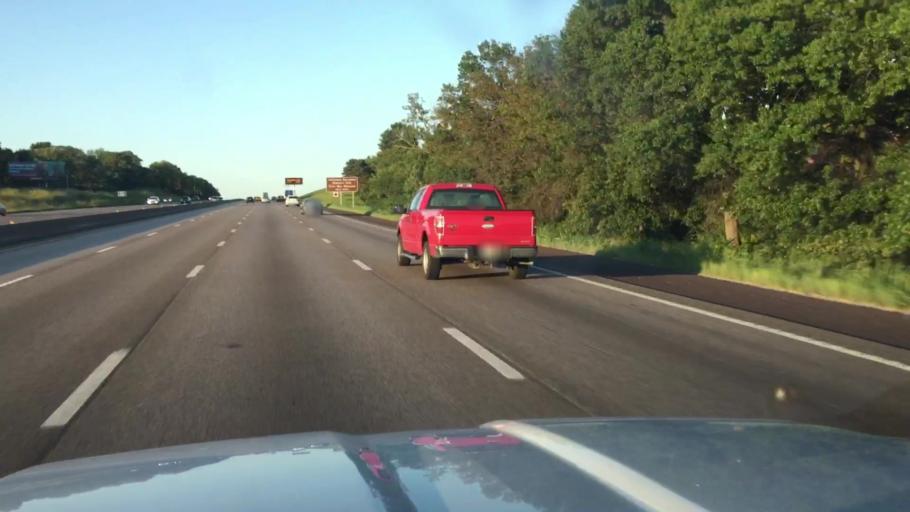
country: US
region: Missouri
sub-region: Saint Louis County
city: Saint George
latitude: 38.5260
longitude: -90.3183
